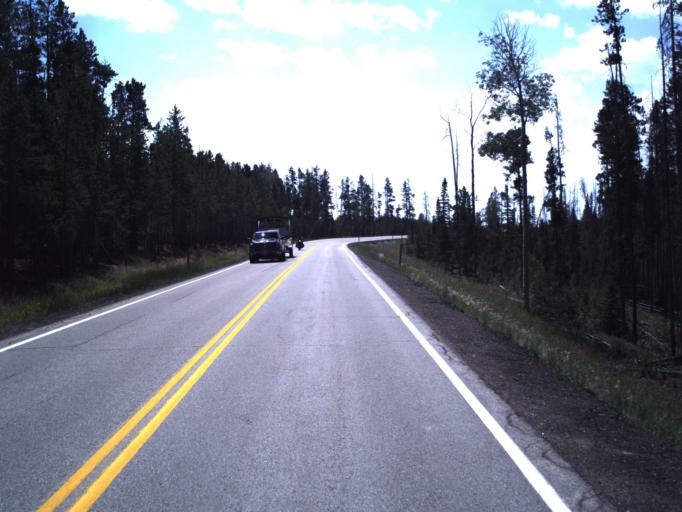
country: US
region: Utah
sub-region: Uintah County
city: Maeser
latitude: 40.7580
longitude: -109.4706
